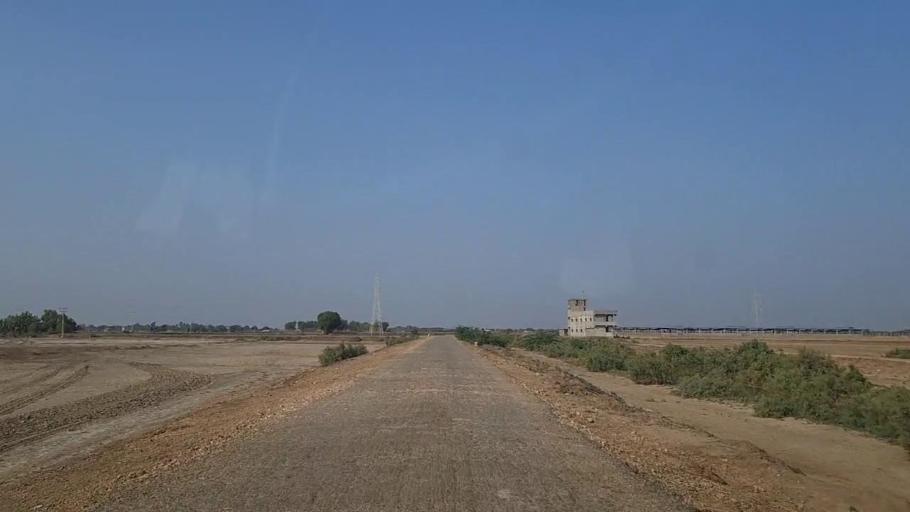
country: PK
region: Sindh
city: Mirpur Sakro
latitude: 24.5610
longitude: 67.6708
